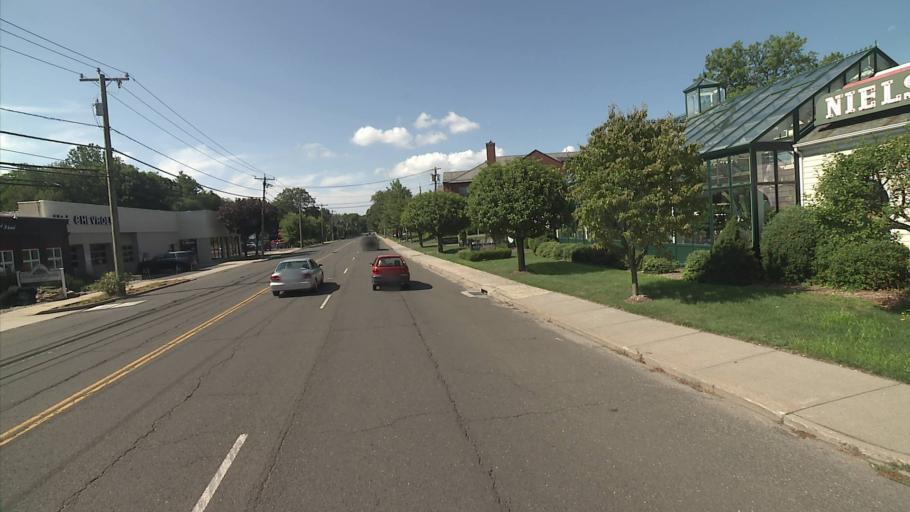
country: US
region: Connecticut
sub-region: Fairfield County
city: Darien
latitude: 41.0693
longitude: -73.4774
